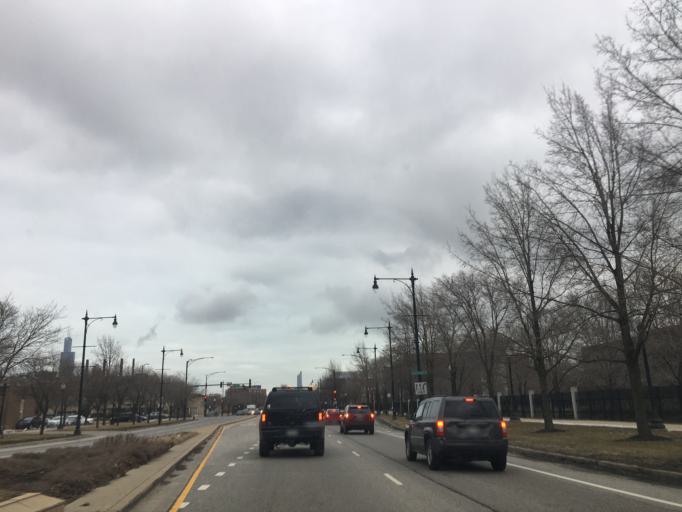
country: US
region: Illinois
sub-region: Cook County
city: Chicago
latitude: 41.8667
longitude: -87.6779
